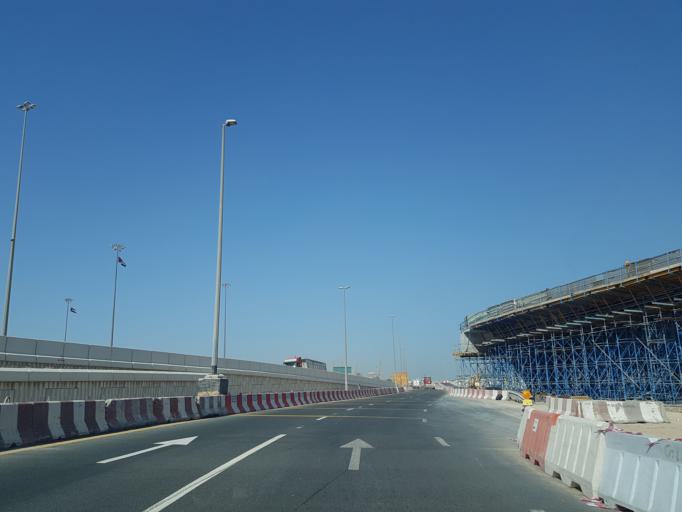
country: AE
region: Dubai
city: Dubai
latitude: 25.0137
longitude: 55.0913
